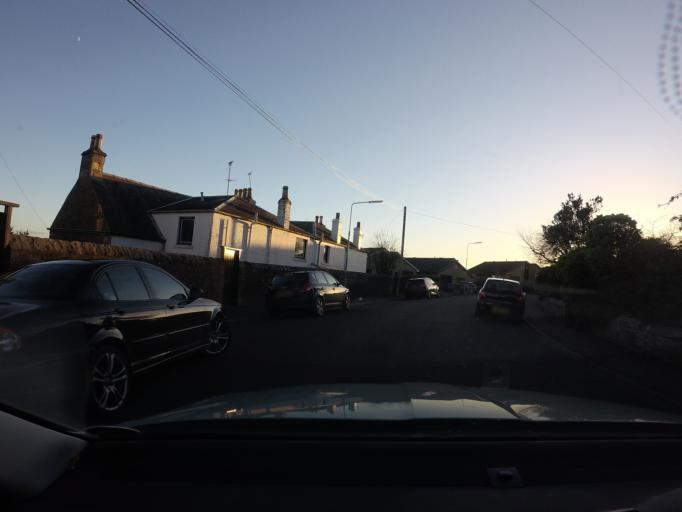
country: GB
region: Scotland
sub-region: Fife
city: Tayport
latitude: 56.4473
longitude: -2.8841
